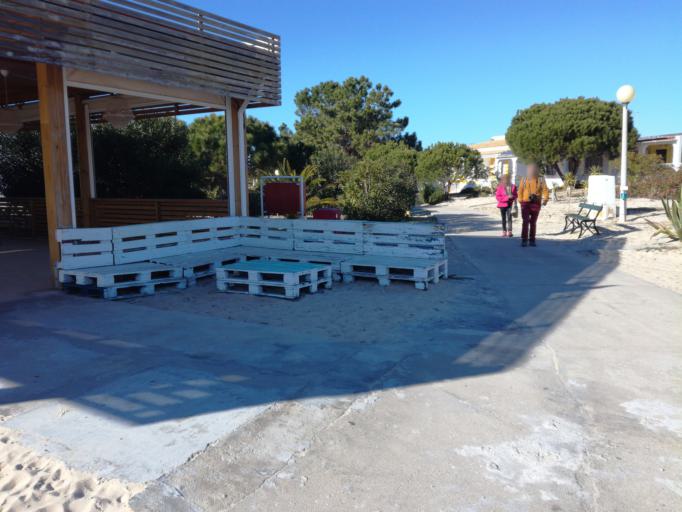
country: PT
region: Faro
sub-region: Olhao
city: Olhao
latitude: 37.0164
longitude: -7.7974
